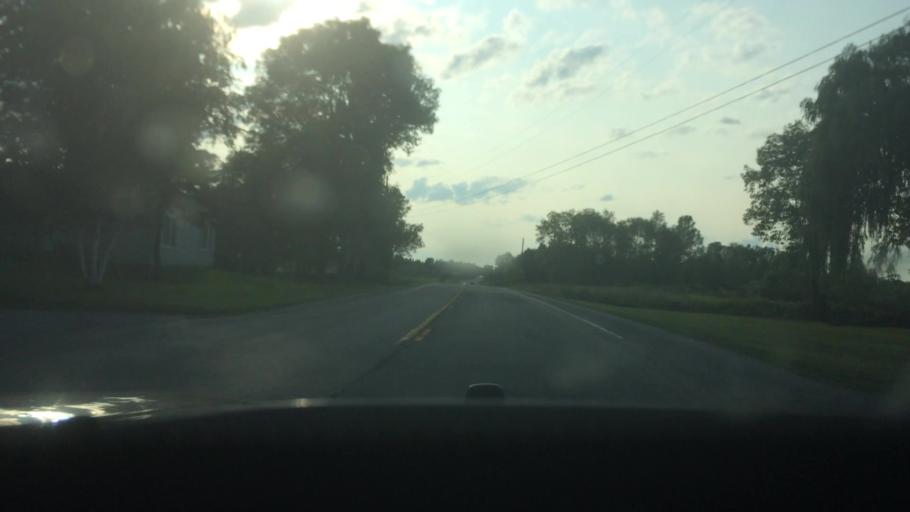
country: US
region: New York
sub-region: St. Lawrence County
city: Ogdensburg
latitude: 44.6714
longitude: -75.3854
